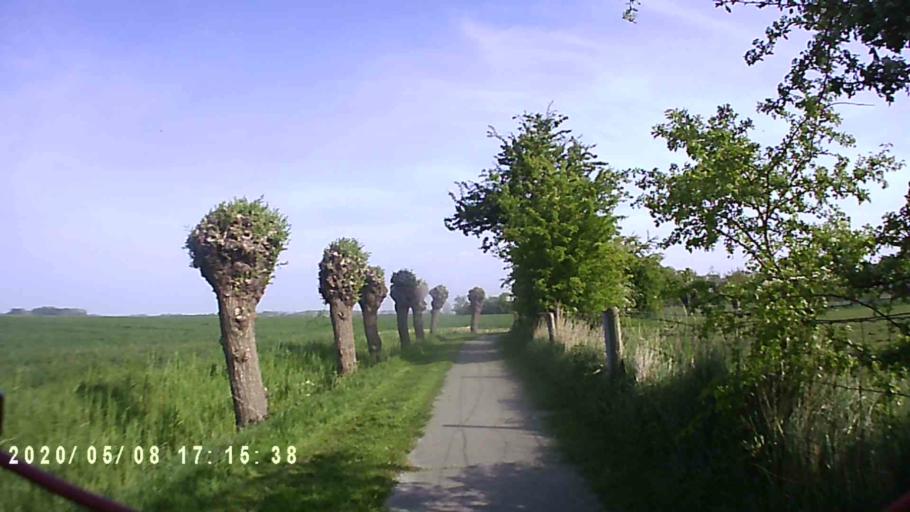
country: NL
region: Groningen
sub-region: Gemeente Winsum
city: Winsum
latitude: 53.3938
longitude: 6.5647
